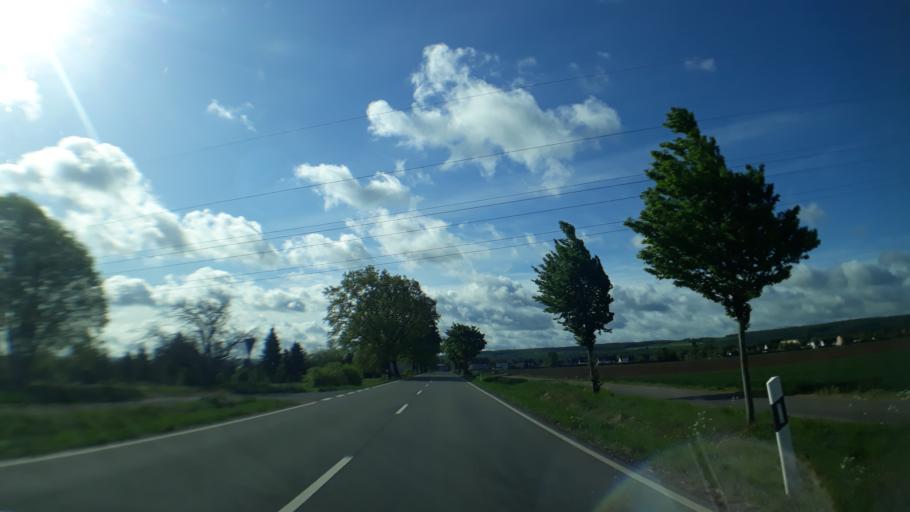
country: DE
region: North Rhine-Westphalia
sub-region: Regierungsbezirk Koln
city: Euskirchen
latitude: 50.6583
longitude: 6.7455
